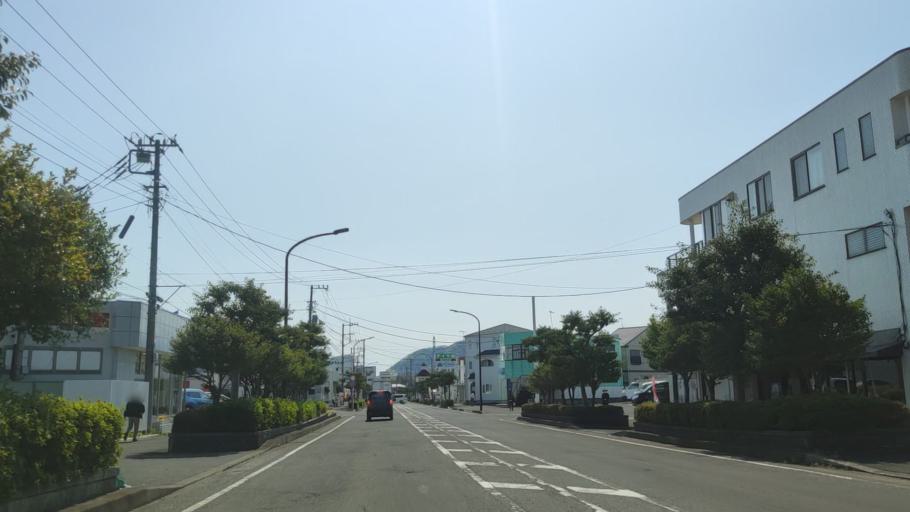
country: JP
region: Kanagawa
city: Oiso
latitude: 35.3376
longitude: 139.3051
